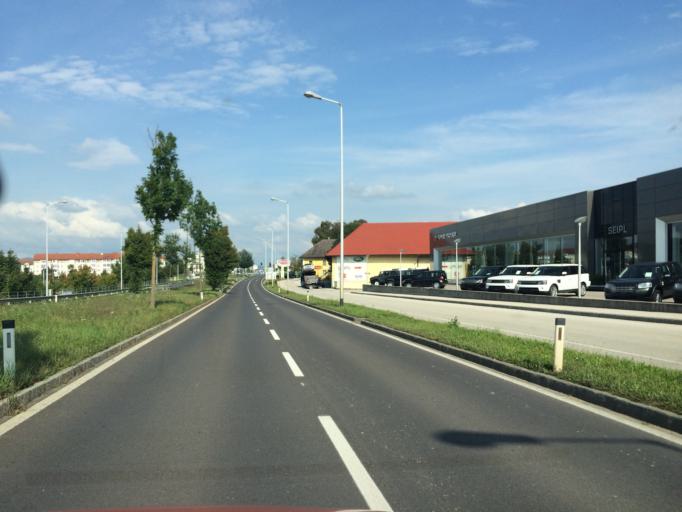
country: AT
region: Upper Austria
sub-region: Politischer Bezirk Linz-Land
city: Leonding
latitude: 48.2546
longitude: 14.2489
